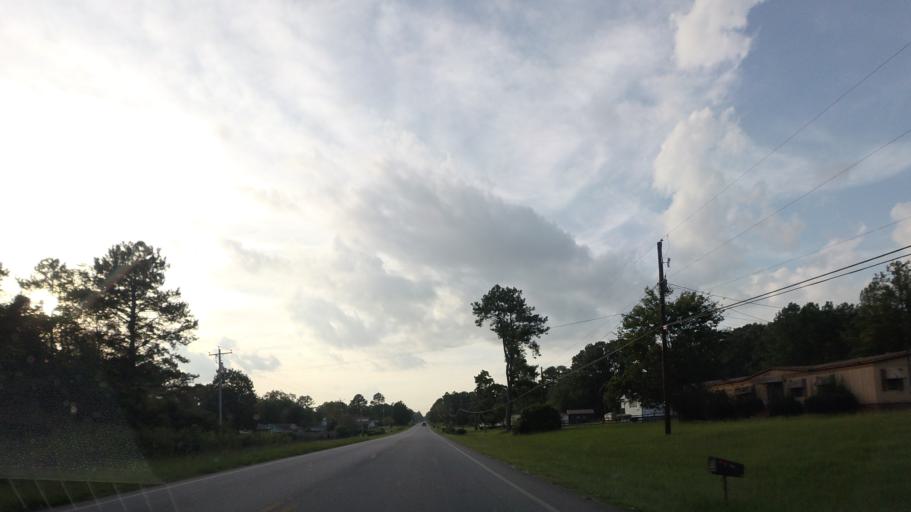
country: US
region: Georgia
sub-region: Wilkinson County
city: Gordon
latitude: 32.8908
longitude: -83.3544
